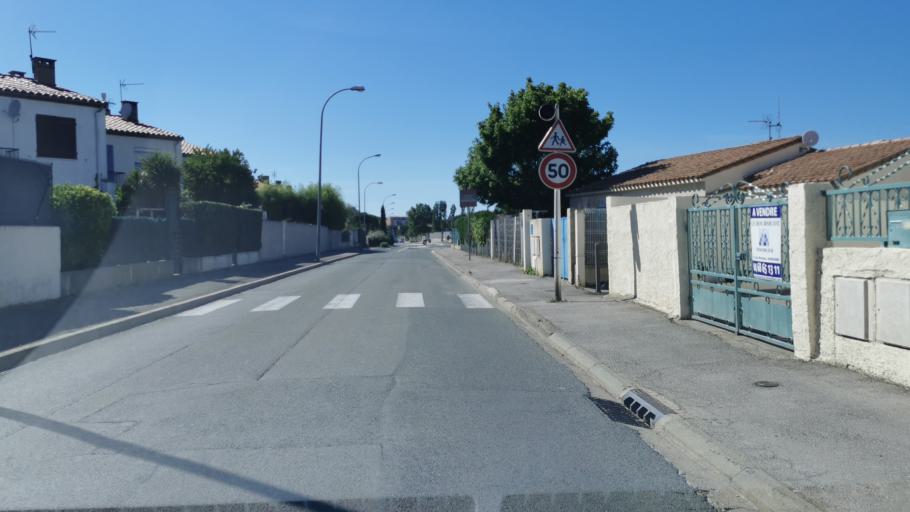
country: FR
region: Languedoc-Roussillon
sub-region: Departement de l'Aude
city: Narbonne
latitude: 43.1923
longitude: 3.0204
